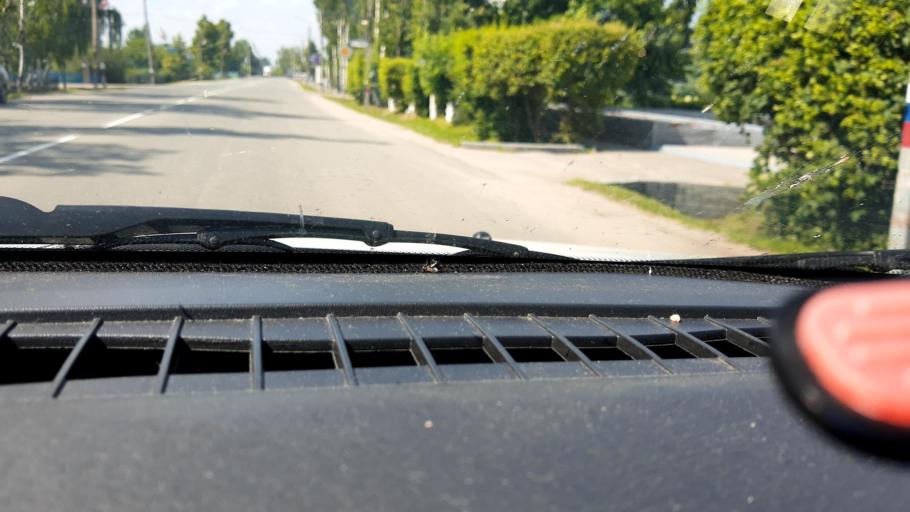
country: RU
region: Nizjnij Novgorod
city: Sharanga
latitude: 57.1780
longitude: 46.5416
